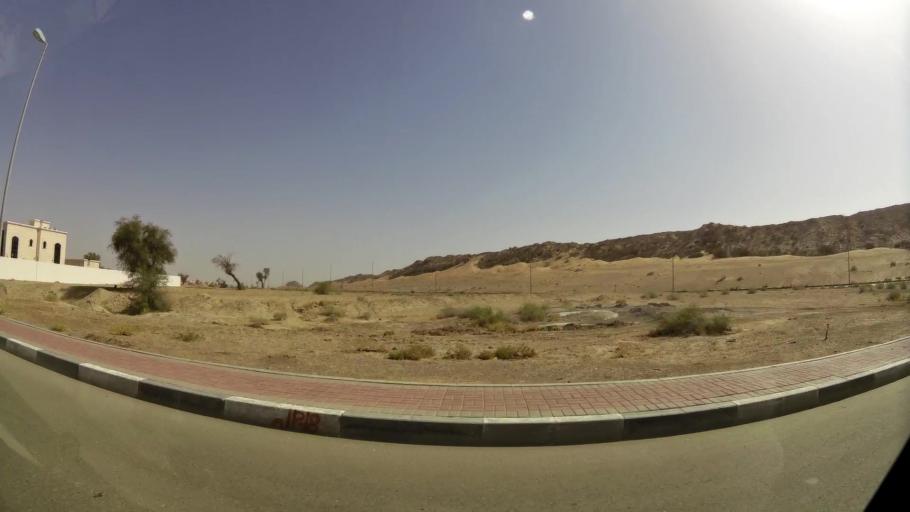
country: OM
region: Al Buraimi
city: Al Buraymi
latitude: 24.3210
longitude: 55.8125
